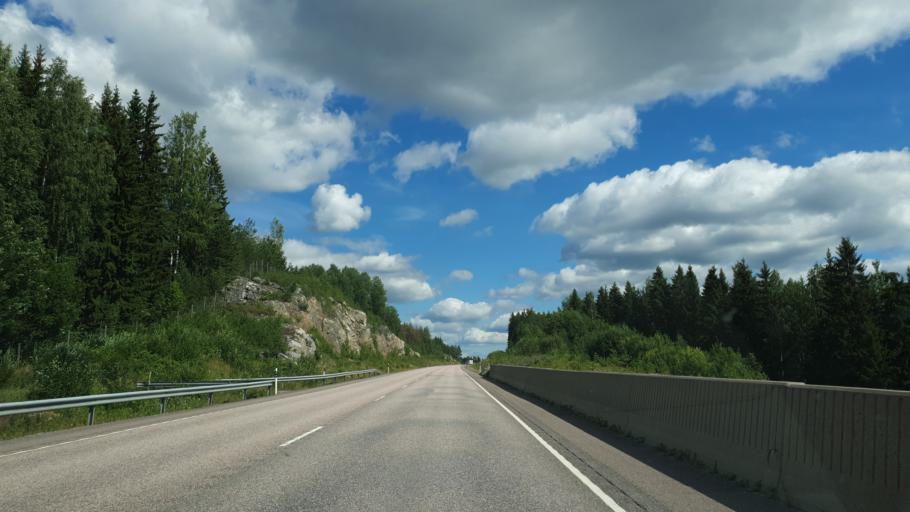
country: FI
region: Pirkanmaa
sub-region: Tampere
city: Kuhmalahti
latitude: 61.7086
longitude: 24.6013
